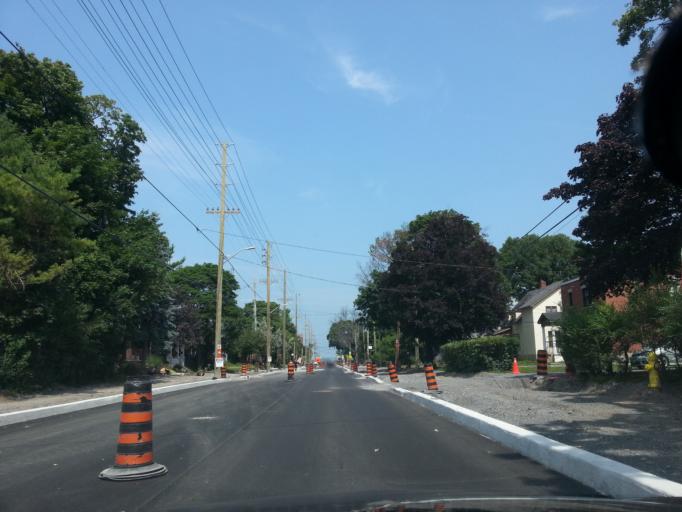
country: CA
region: Ontario
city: Ottawa
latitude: 45.3879
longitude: -75.7512
